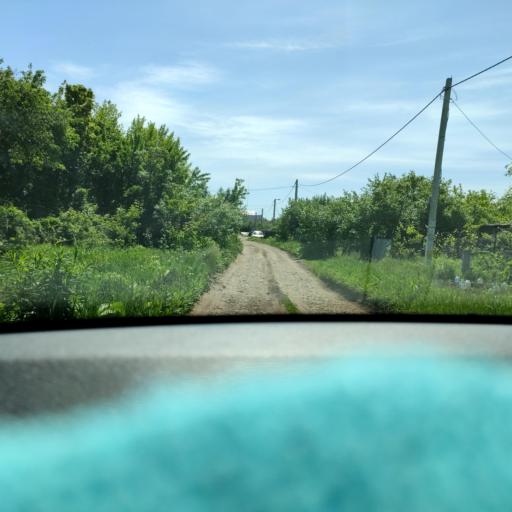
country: RU
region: Samara
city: Petra-Dubrava
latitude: 53.2901
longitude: 50.2979
